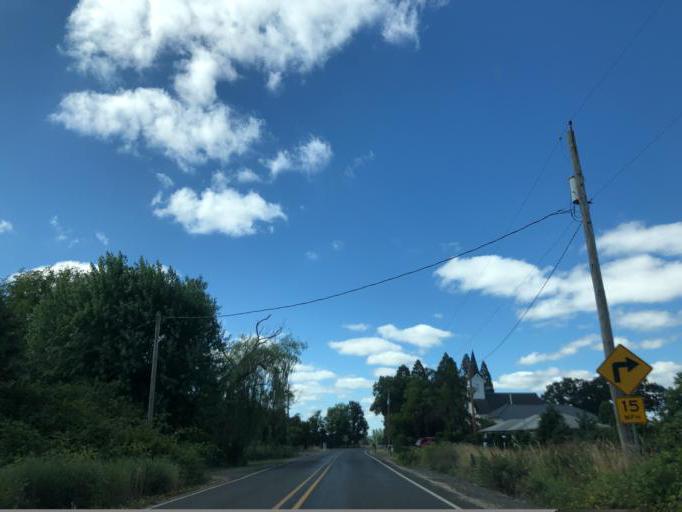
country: US
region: Oregon
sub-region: Marion County
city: Mount Angel
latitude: 45.1016
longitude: -122.7313
